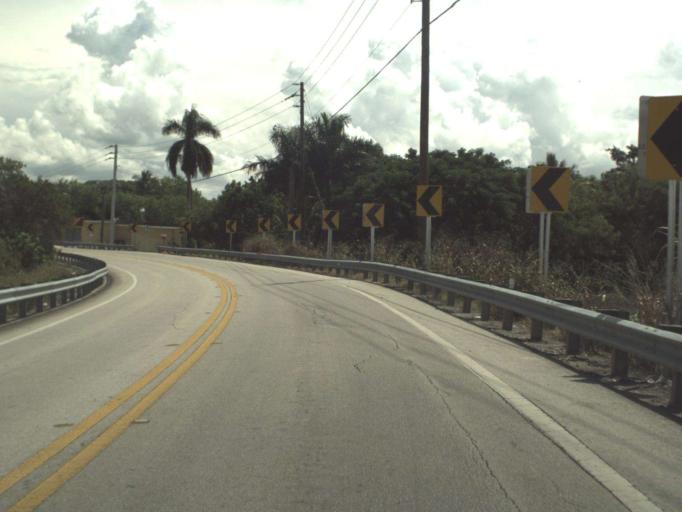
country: US
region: Florida
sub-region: Palm Beach County
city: Pahokee
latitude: 26.8133
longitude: -80.6651
